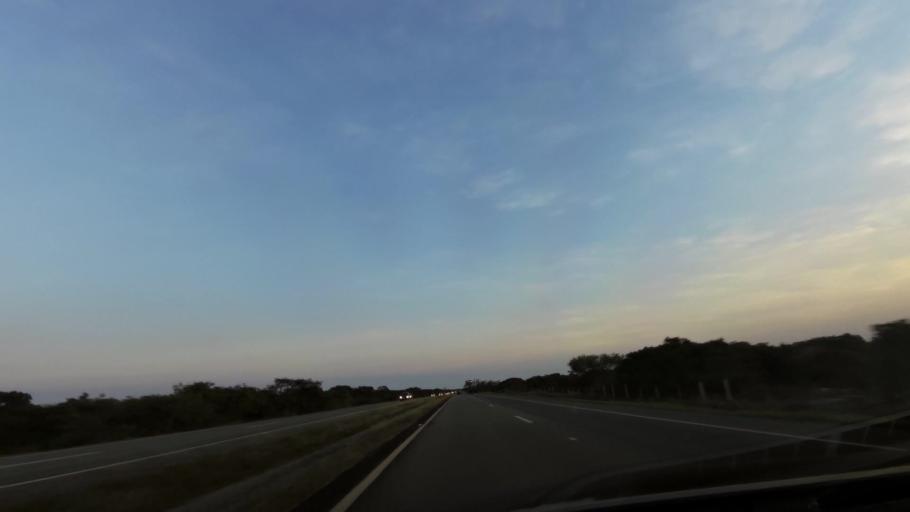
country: BR
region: Espirito Santo
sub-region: Guarapari
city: Guarapari
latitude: -20.5901
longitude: -40.4252
